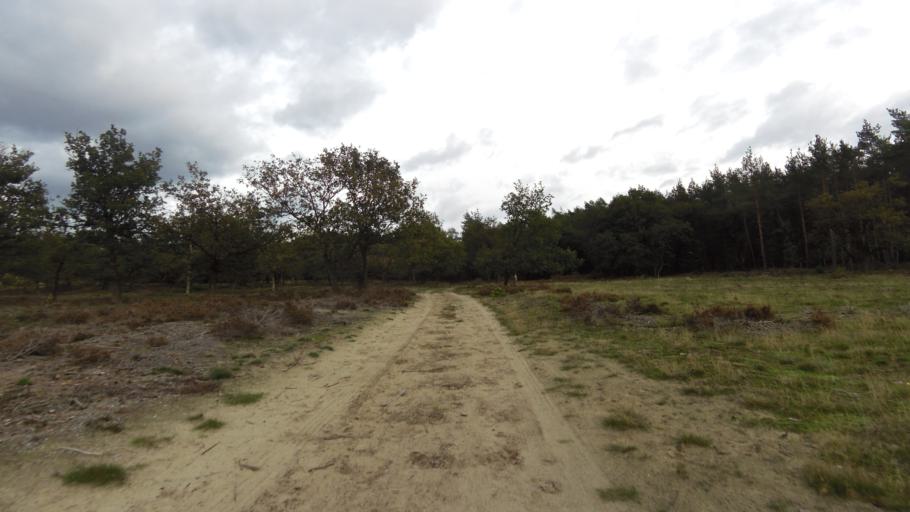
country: NL
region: Gelderland
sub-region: Gemeente Barneveld
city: Stroe
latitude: 52.1810
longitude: 5.7268
